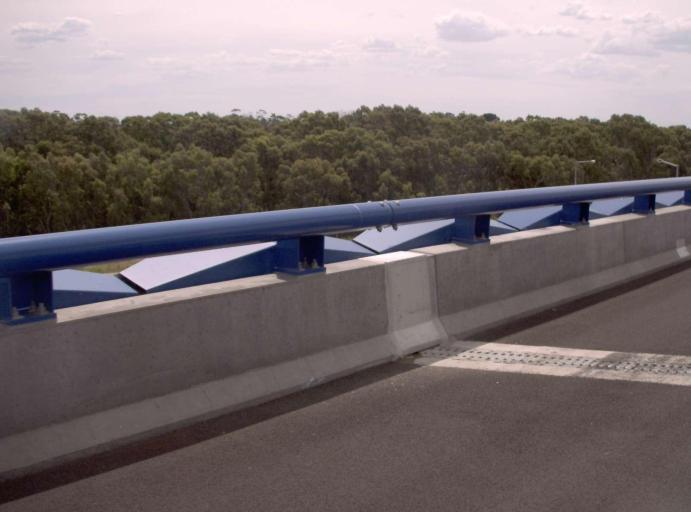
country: AU
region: Victoria
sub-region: Kingston
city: Carrum
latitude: -38.0916
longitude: 145.1522
